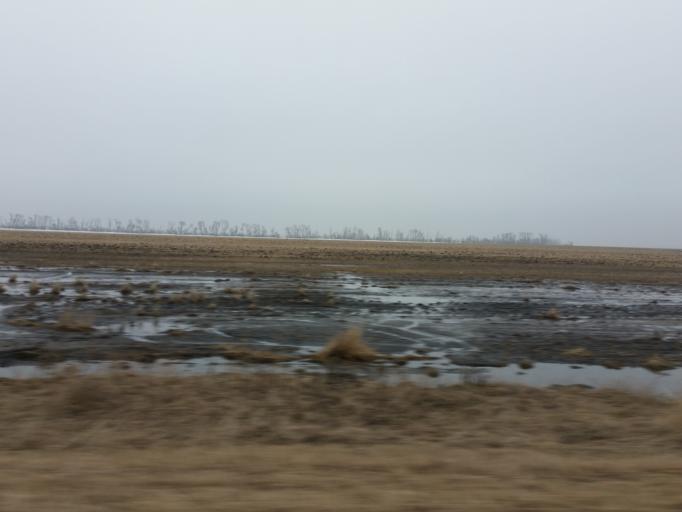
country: US
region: North Dakota
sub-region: Walsh County
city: Grafton
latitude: 48.4157
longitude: -97.3646
